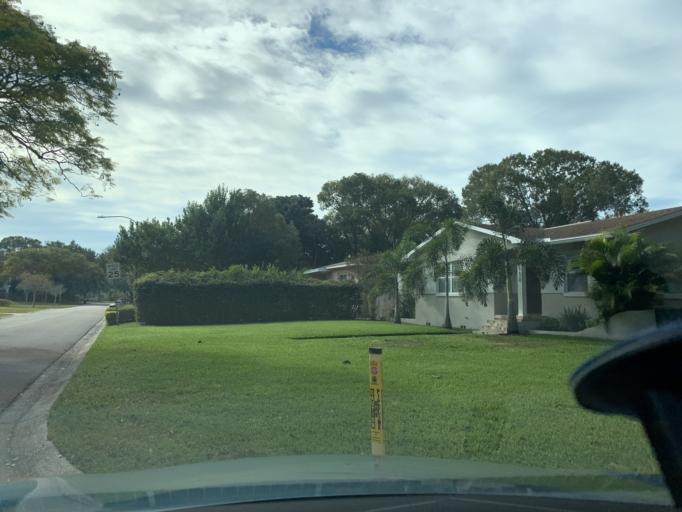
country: US
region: Florida
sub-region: Pinellas County
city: Saint Petersburg
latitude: 27.7956
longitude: -82.6582
